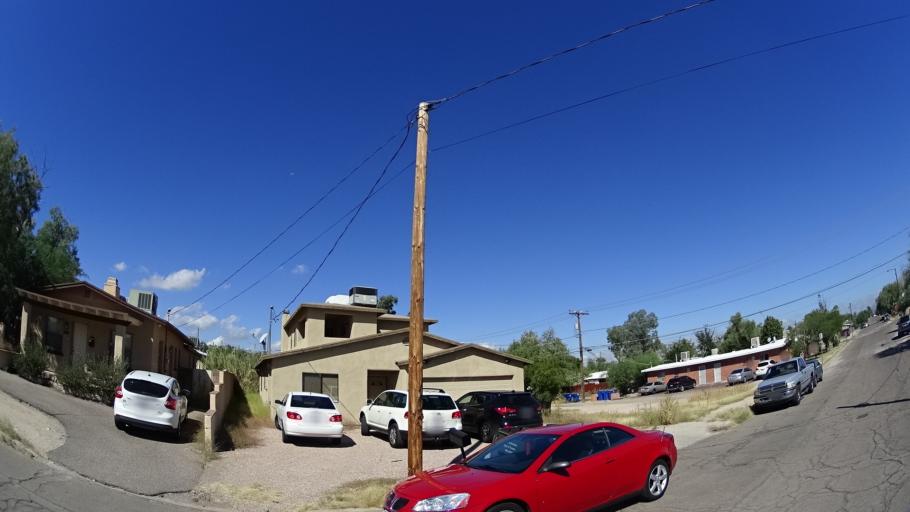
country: US
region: Arizona
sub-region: Pima County
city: Tucson
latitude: 32.2418
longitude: -110.9553
